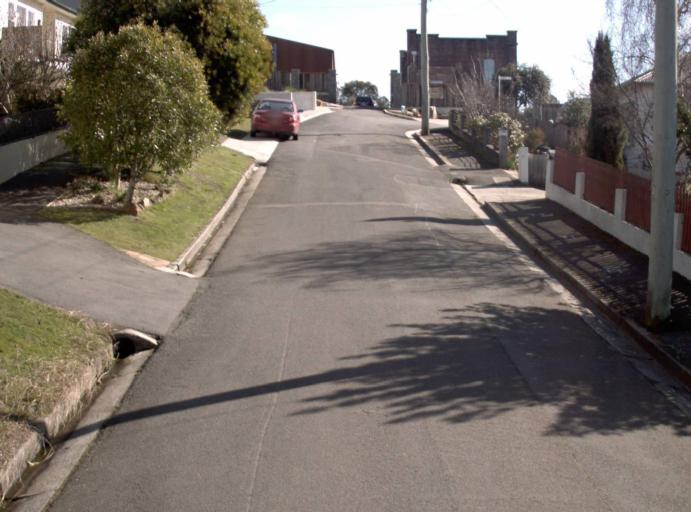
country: AU
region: Tasmania
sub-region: Launceston
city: West Launceston
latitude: -41.4441
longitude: 147.1263
